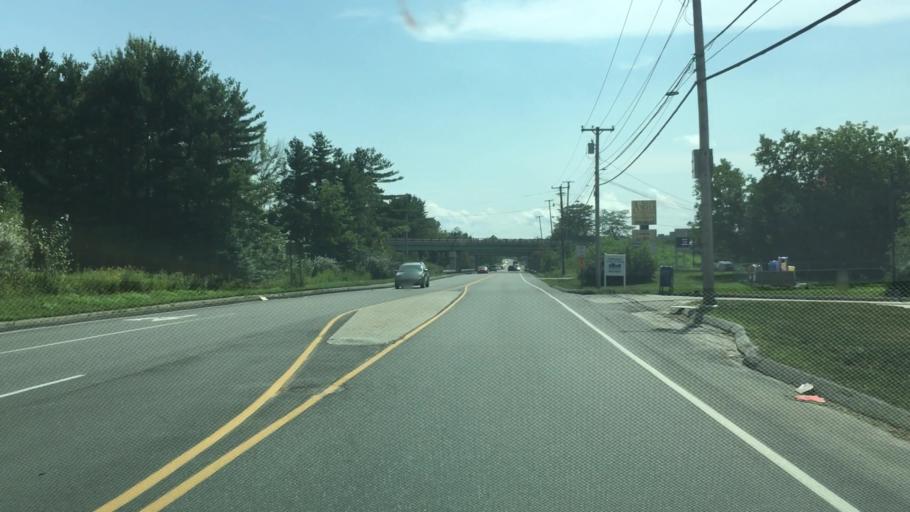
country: US
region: Maine
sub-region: Penobscot County
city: Brewer
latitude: 44.8256
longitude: -68.7577
